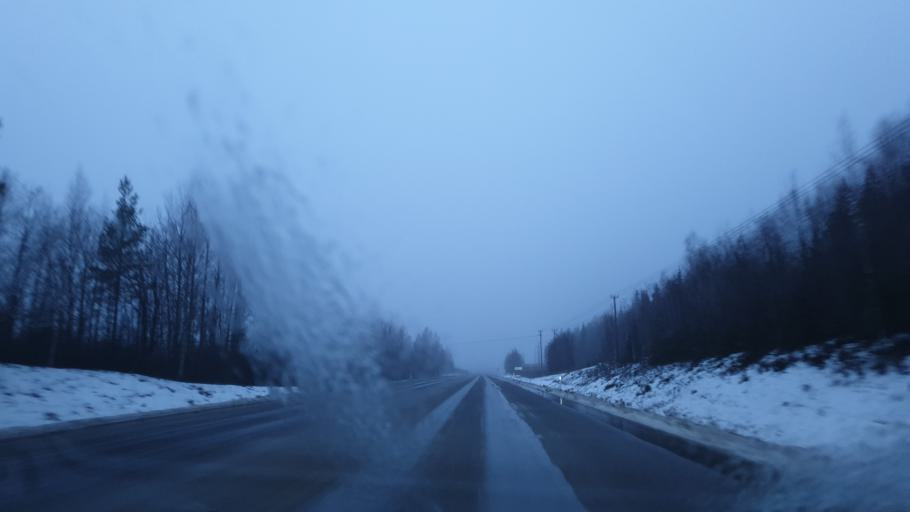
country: SE
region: Vaesterbotten
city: Obbola
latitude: 63.7744
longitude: 20.3304
